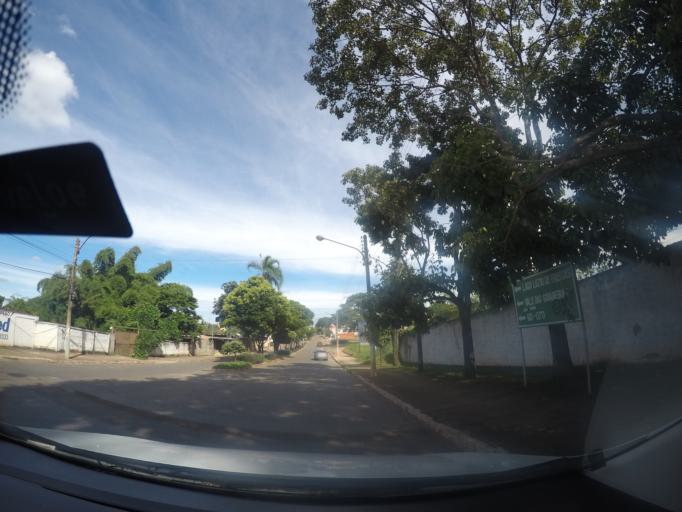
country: BR
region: Goias
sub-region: Inhumas
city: Inhumas
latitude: -16.3659
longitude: -49.4988
